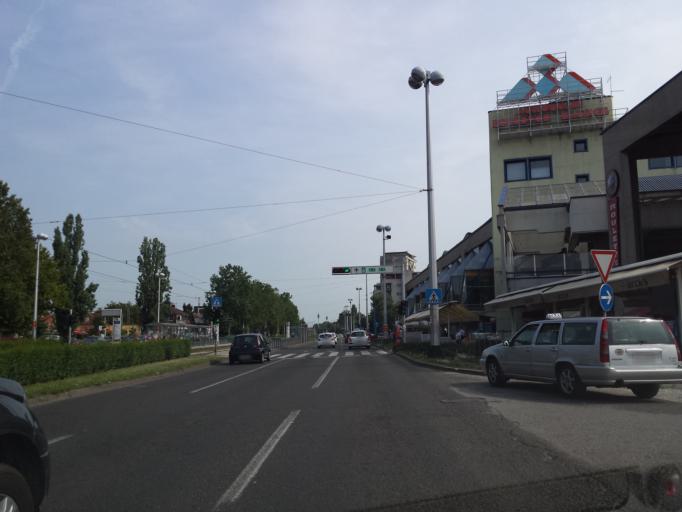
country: HR
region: Grad Zagreb
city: Zagreb - Centar
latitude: 45.8047
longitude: 15.9932
